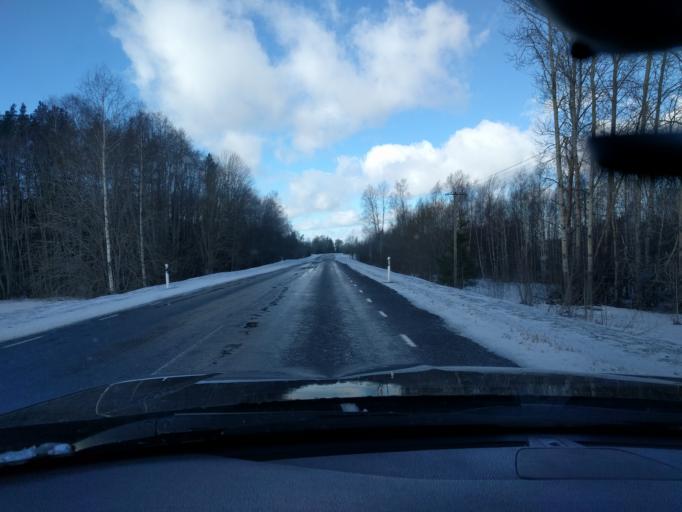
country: EE
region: Harju
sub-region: Anija vald
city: Kehra
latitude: 59.2249
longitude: 25.4025
